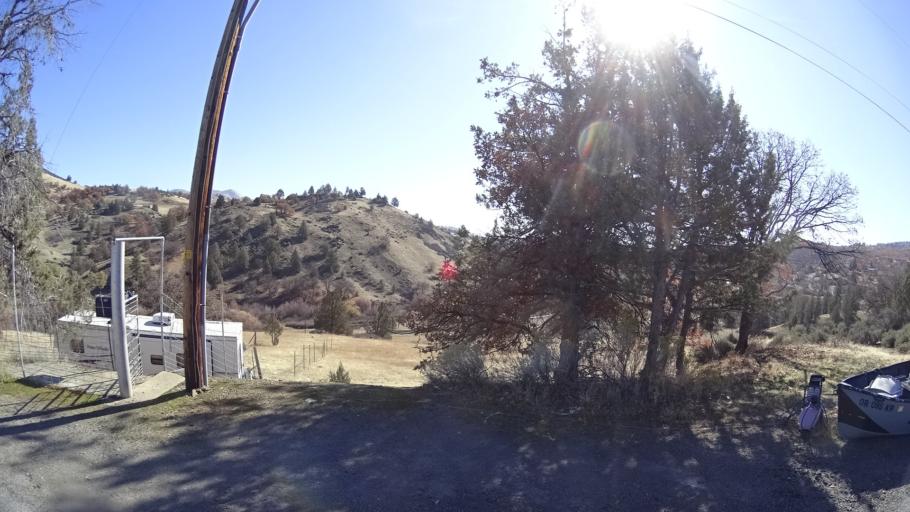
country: US
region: California
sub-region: Siskiyou County
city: Montague
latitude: 41.8792
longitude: -122.4778
